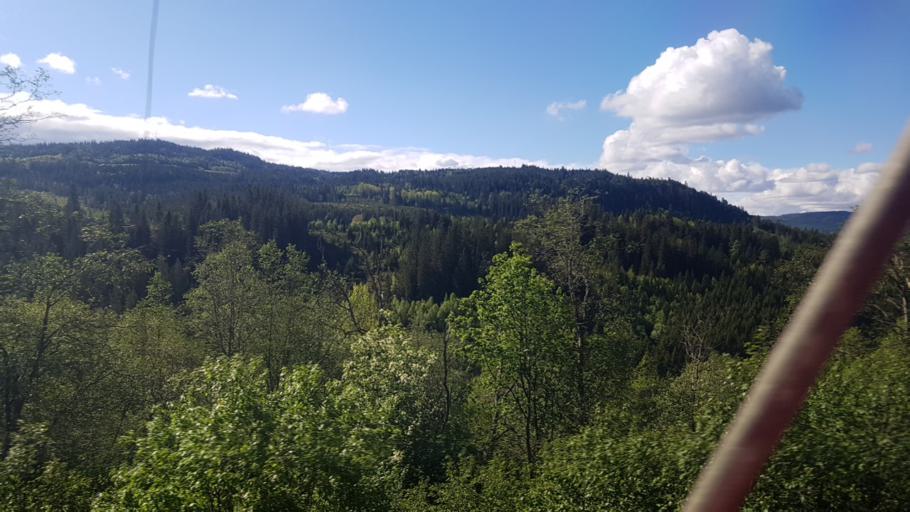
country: NO
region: Sor-Trondelag
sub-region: Midtre Gauldal
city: Storen
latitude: 62.9696
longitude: 10.2035
